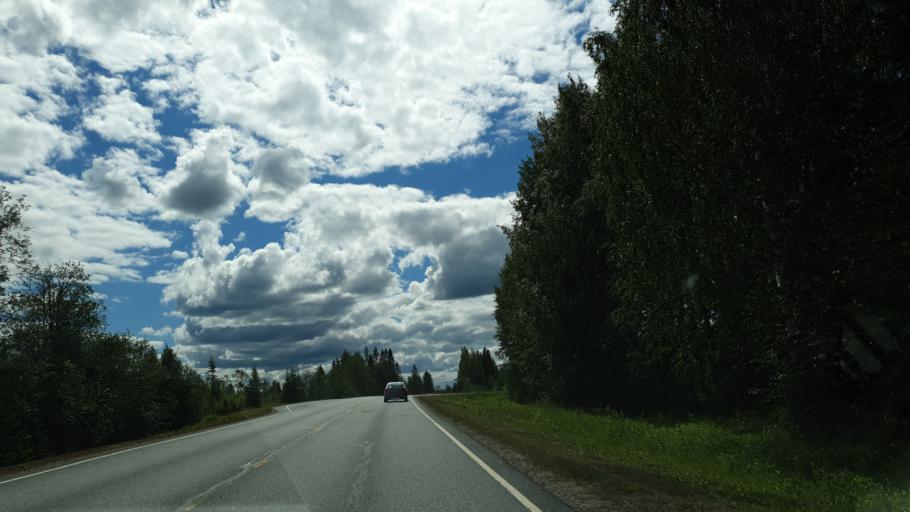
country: FI
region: North Karelia
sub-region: Pielisen Karjala
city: Valtimo
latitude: 63.4069
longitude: 28.7760
